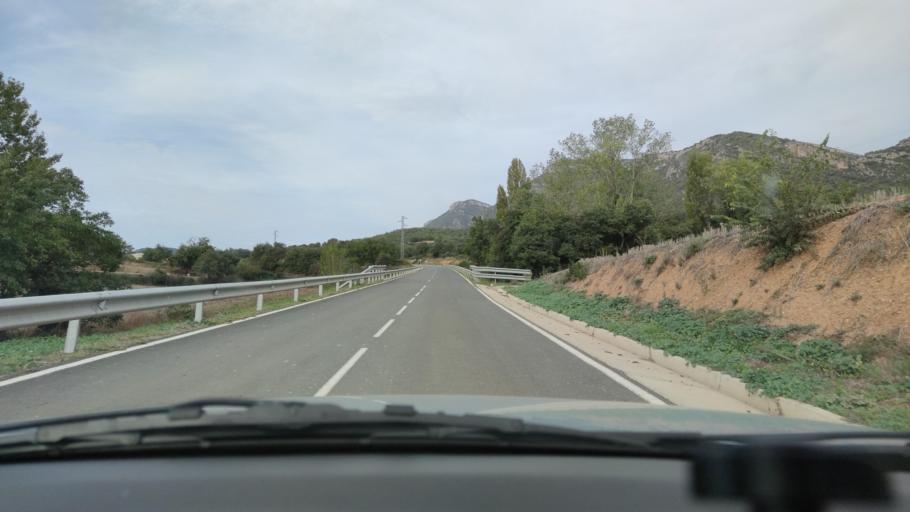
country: ES
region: Catalonia
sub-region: Provincia de Lleida
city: Artesa de Segre
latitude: 41.9930
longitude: 1.0153
